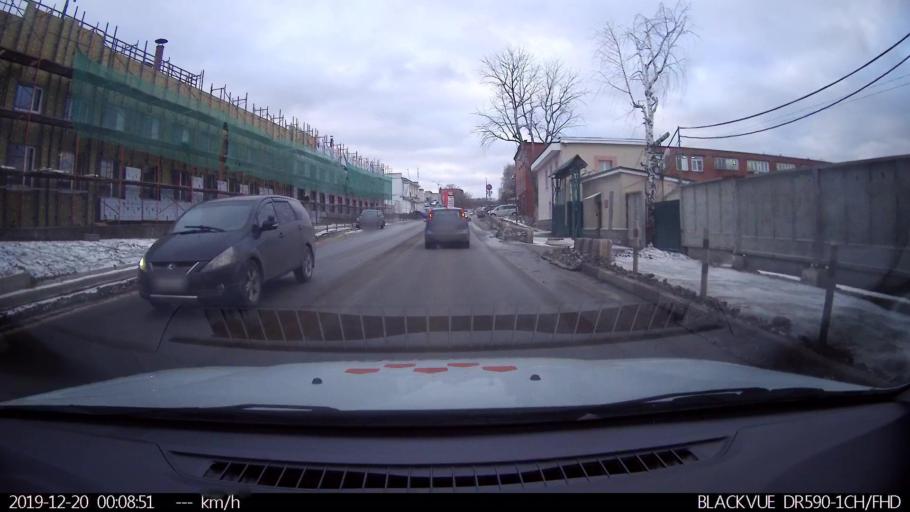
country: RU
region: Jaroslavl
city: Yaroslavl
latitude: 57.7303
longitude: 39.7452
